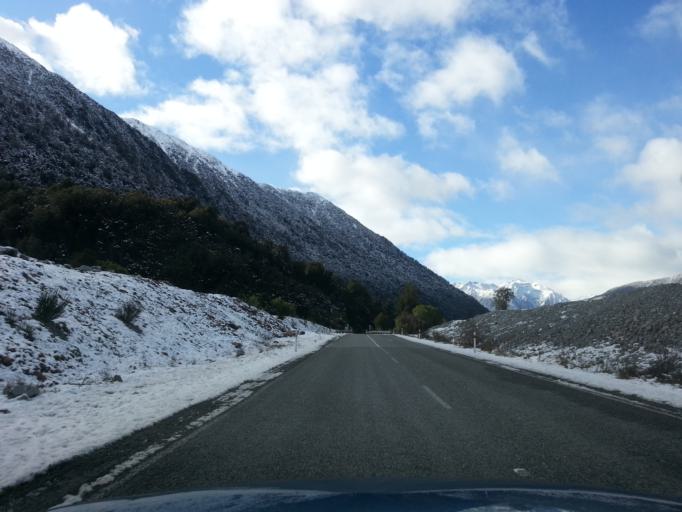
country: NZ
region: West Coast
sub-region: Grey District
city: Greymouth
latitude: -42.8049
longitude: 171.5728
